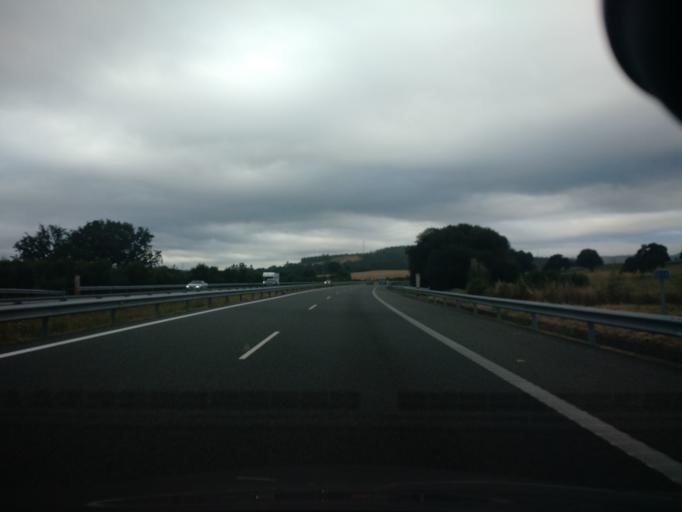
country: ES
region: Galicia
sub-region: Provincia da Coruna
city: Abegondo
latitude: 43.2434
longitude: -8.2564
